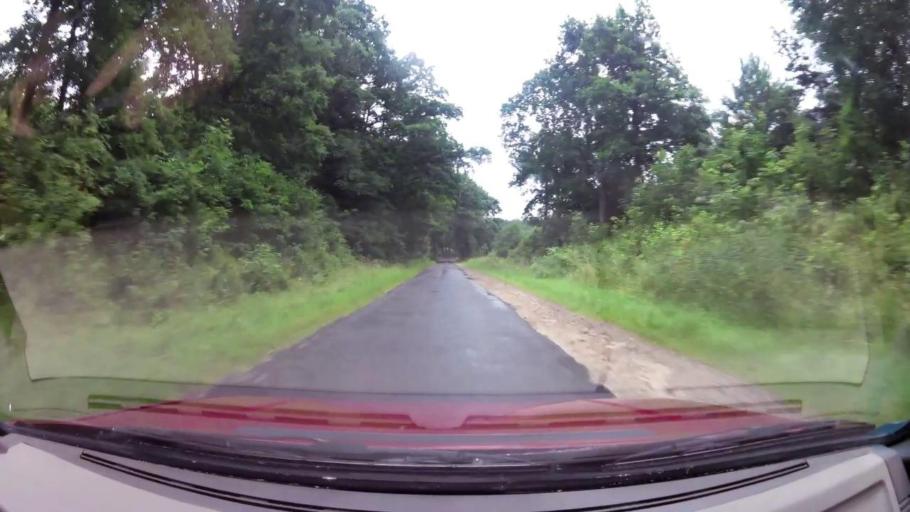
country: PL
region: West Pomeranian Voivodeship
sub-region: Powiat swidwinski
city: Rabino
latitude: 53.9325
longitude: 15.9640
